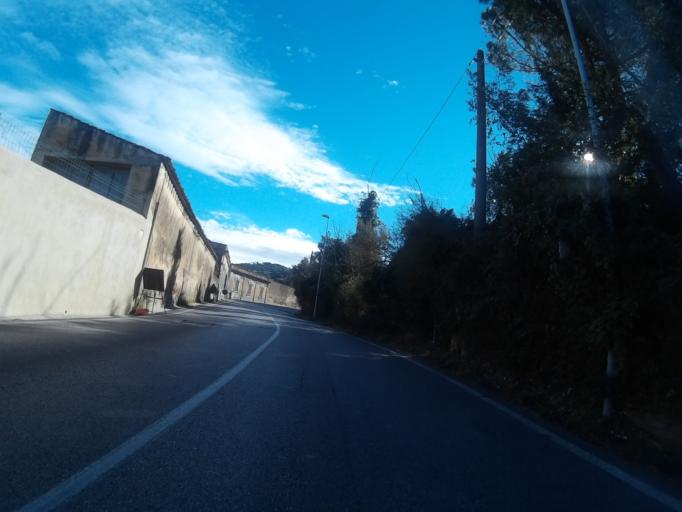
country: IT
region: Tuscany
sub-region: Provincia di Livorno
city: Livorno
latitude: 43.5014
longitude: 10.3409
